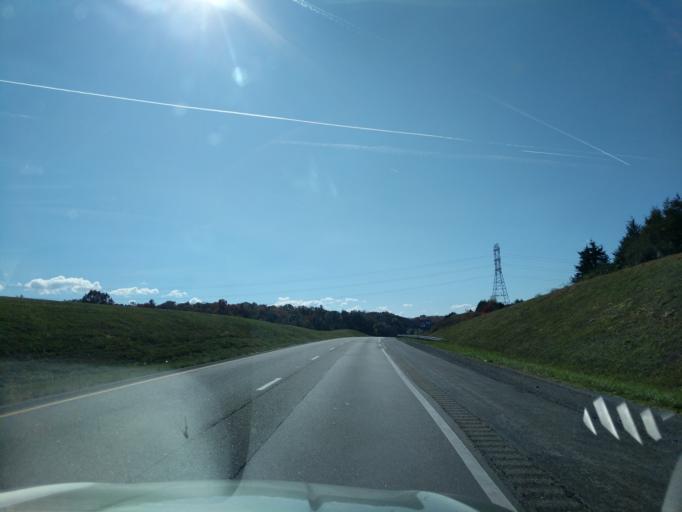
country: US
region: Virginia
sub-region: City of Staunton
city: Staunton
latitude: 38.1474
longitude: -79.0181
